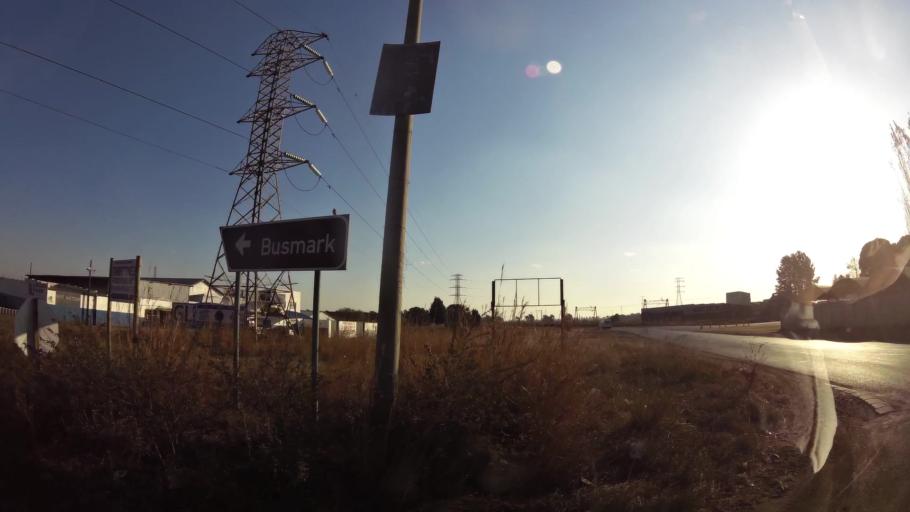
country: ZA
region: Gauteng
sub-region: West Rand District Municipality
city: Randfontein
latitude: -26.1922
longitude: 27.6869
